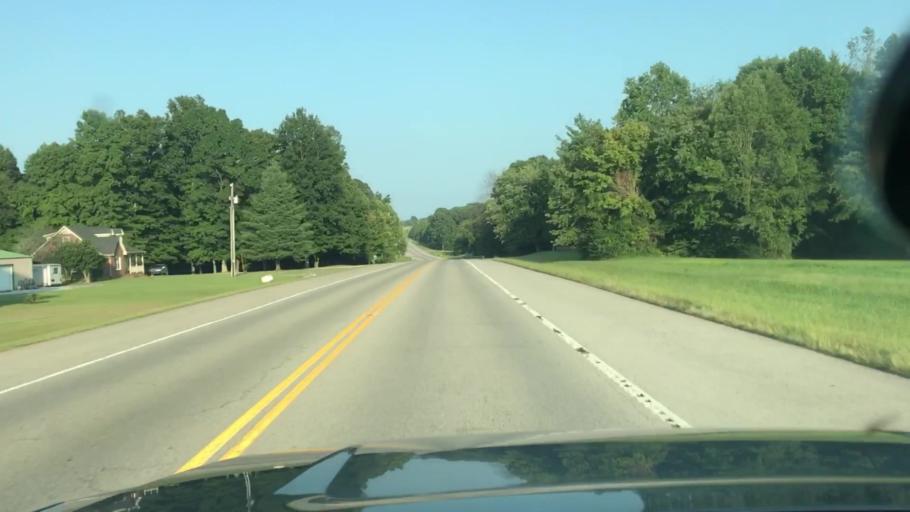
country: US
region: Tennessee
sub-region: Sumner County
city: Portland
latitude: 36.5783
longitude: -86.4076
